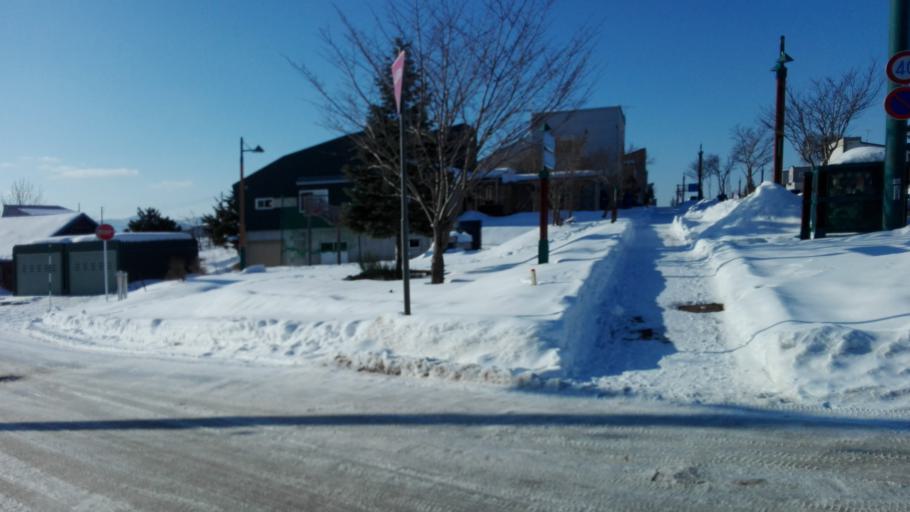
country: JP
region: Hokkaido
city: Niseko Town
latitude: 42.8029
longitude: 140.6893
